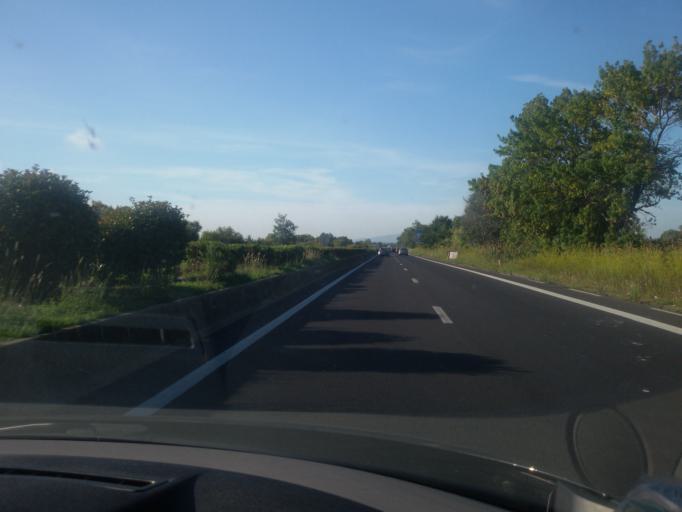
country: FR
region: Languedoc-Roussillon
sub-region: Departement de l'Herault
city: Lattes
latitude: 43.5436
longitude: 3.8964
